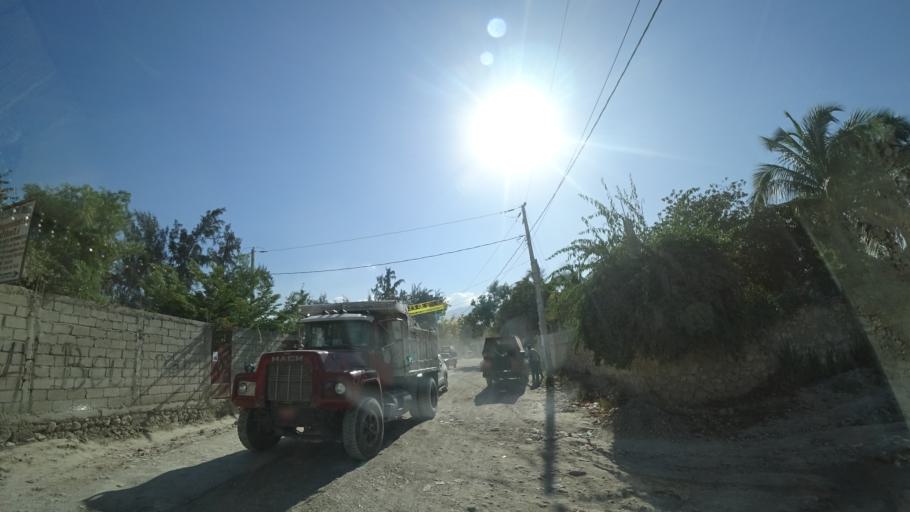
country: HT
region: Ouest
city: Delmas 73
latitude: 18.5546
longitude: -72.2845
